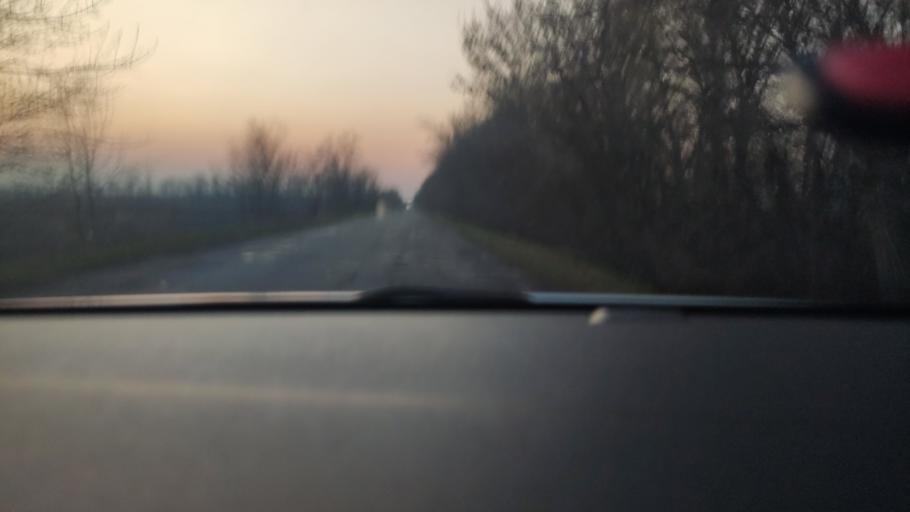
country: RU
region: Voronezj
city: Uryv-Pokrovka
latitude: 51.1393
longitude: 39.0795
